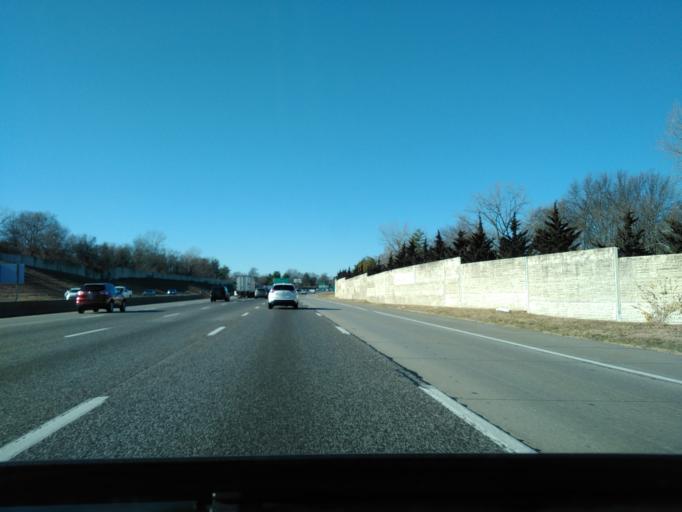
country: US
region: Missouri
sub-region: Saint Louis County
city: Sappington
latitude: 38.5166
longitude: -90.3838
